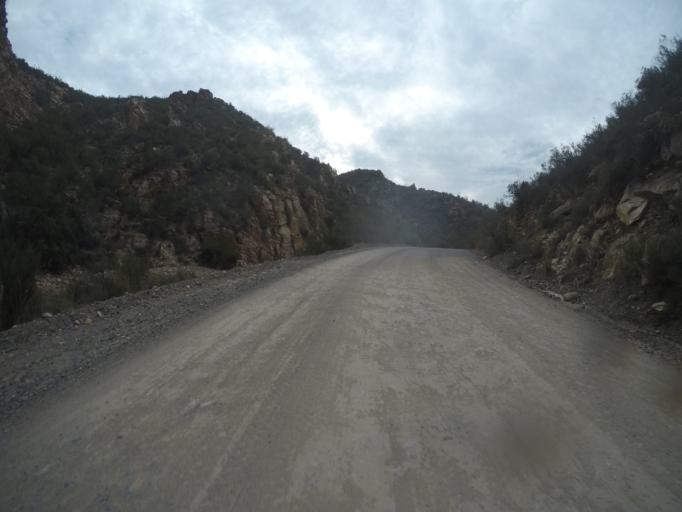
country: ZA
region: Eastern Cape
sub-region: Cacadu District Municipality
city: Willowmore
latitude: -33.5099
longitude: 23.6373
